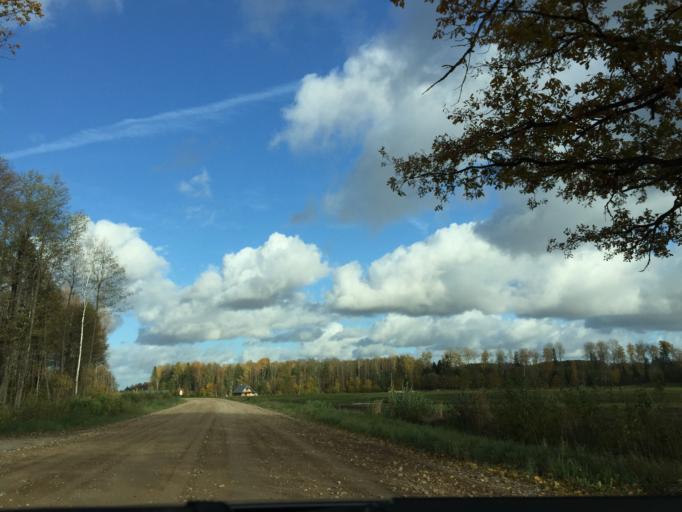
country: LV
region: Ogre
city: Jumprava
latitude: 56.7405
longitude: 24.9015
